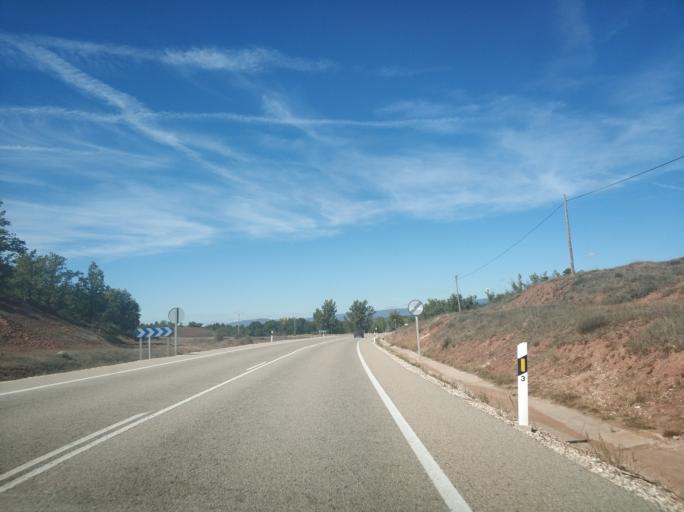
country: ES
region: Castille and Leon
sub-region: Provincia de Burgos
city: Hacinas
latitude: 41.9697
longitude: -3.2959
